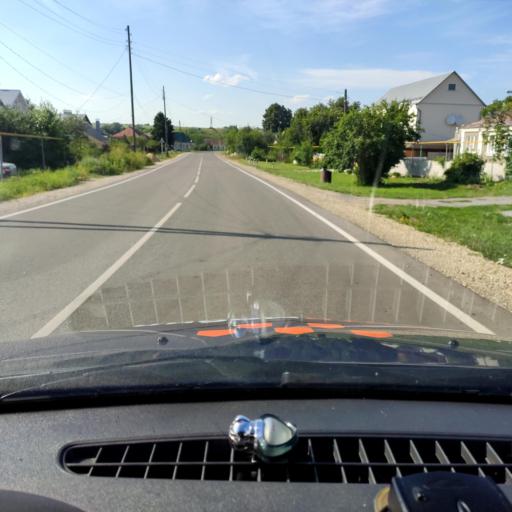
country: RU
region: Voronezj
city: Devitsa
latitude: 51.6540
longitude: 38.9716
